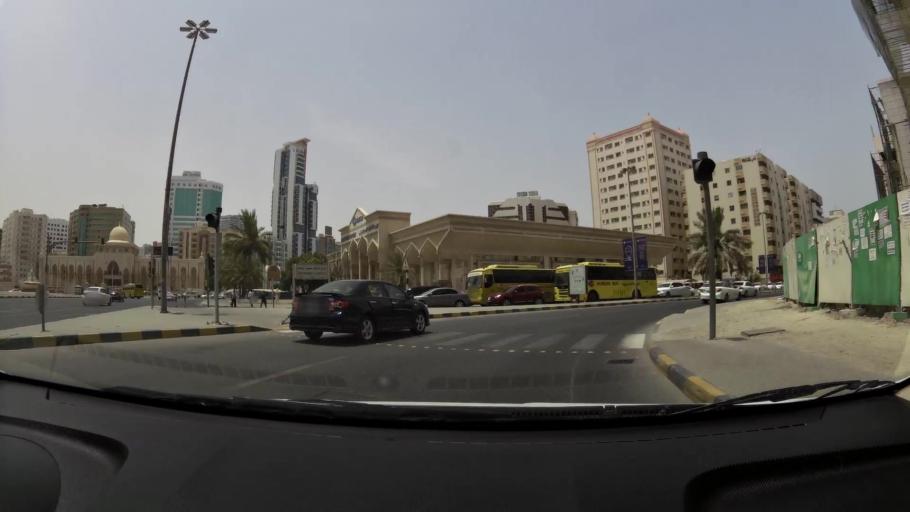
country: AE
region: Ash Shariqah
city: Sharjah
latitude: 25.3529
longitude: 55.3905
